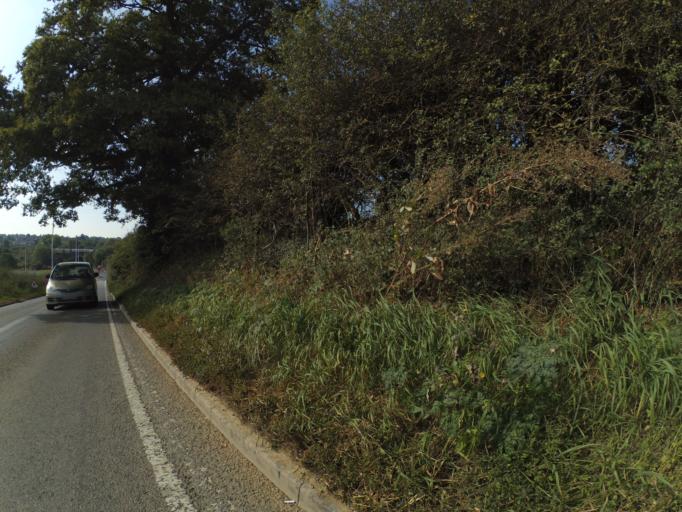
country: GB
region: England
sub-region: Warwickshire
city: Rugby
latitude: 52.3710
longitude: -1.2216
